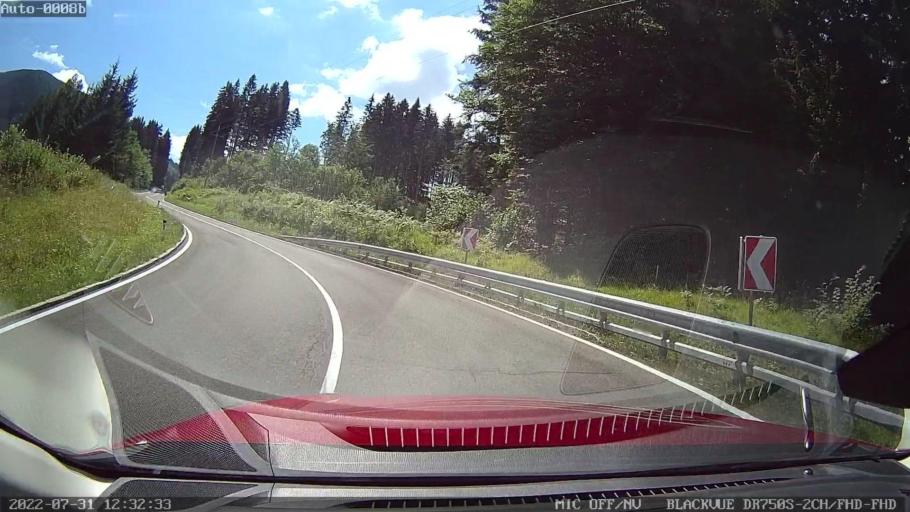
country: AT
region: Carinthia
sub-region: Politischer Bezirk Villach Land
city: Arnoldstein
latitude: 46.5272
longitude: 13.7496
